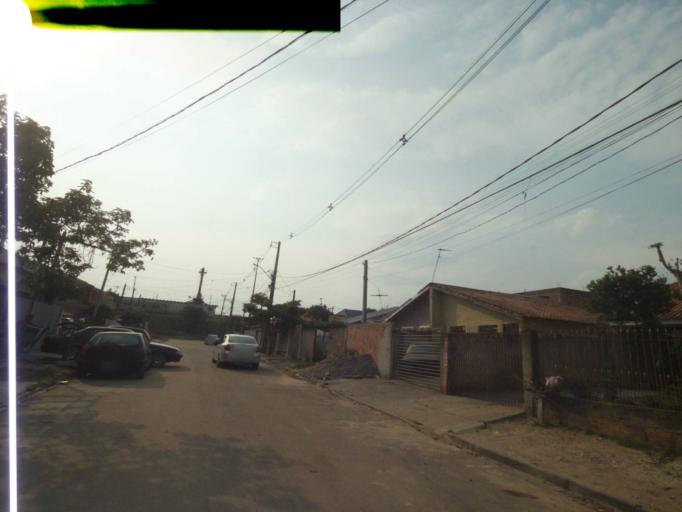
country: BR
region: Parana
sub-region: Sao Jose Dos Pinhais
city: Sao Jose dos Pinhais
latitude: -25.5348
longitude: -49.2309
